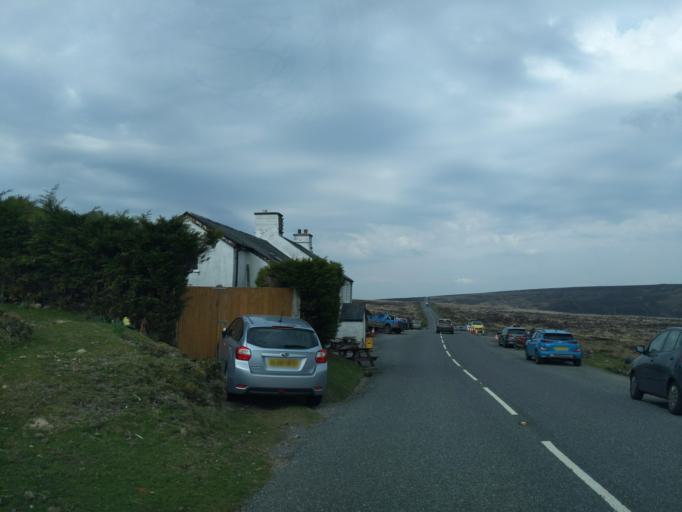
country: GB
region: England
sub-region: Devon
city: Ashburton
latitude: 50.6128
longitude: -3.8753
